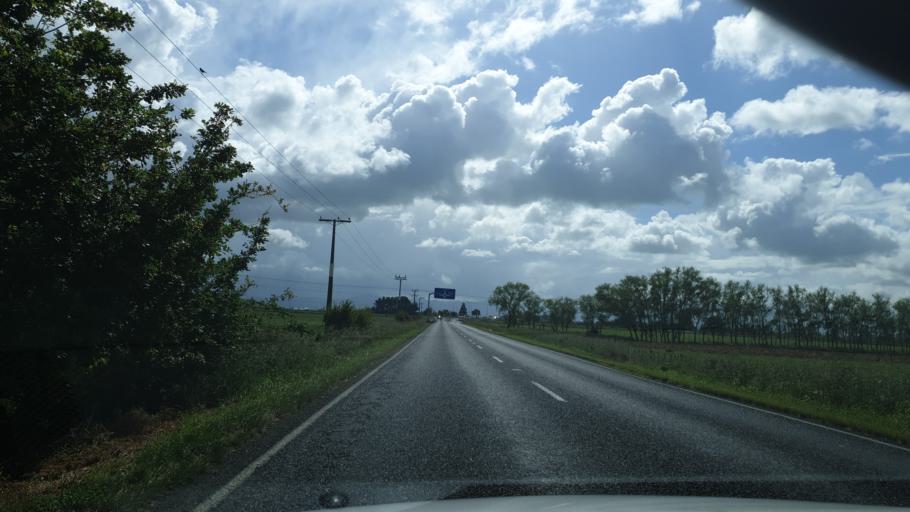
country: NZ
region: Waikato
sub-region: Hauraki District
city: Paeroa
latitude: -37.5115
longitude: 175.5202
